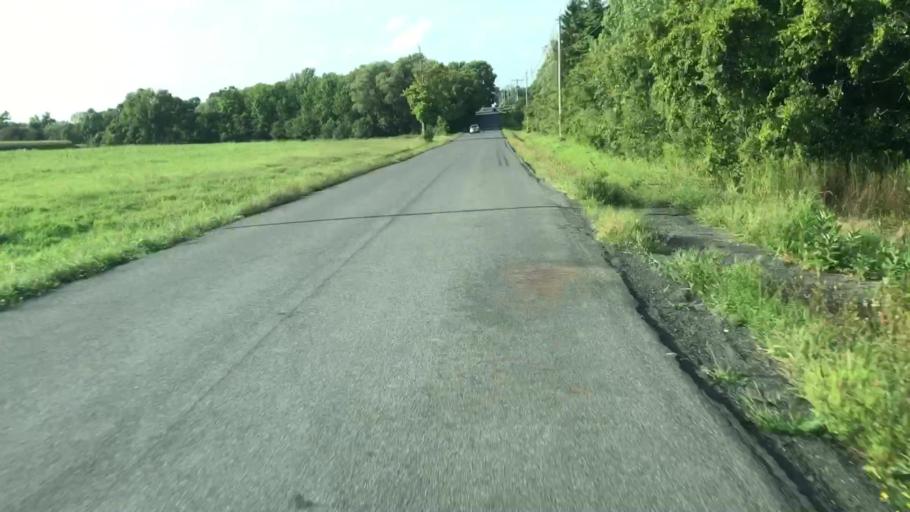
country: US
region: New York
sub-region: Onondaga County
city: Skaneateles
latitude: 42.9549
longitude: -76.4592
